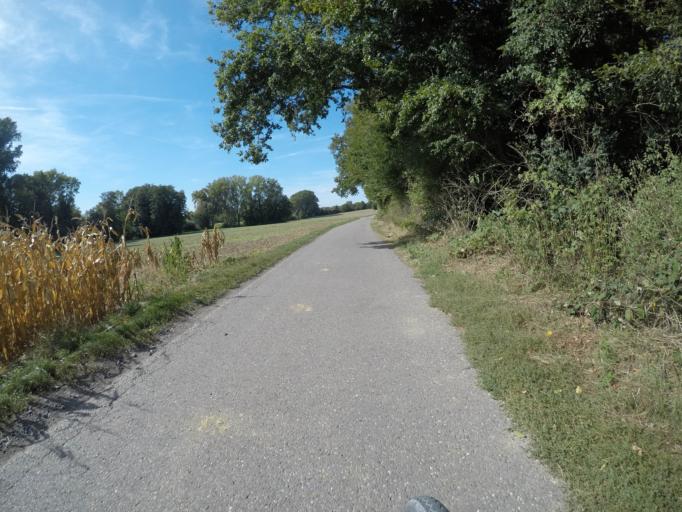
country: DE
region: Baden-Wuerttemberg
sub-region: Karlsruhe Region
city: Ubstadt-Weiher
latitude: 49.1536
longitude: 8.6488
